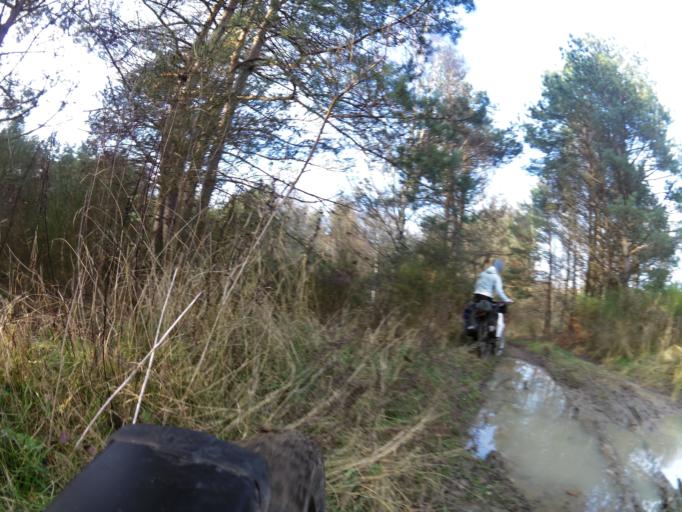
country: PL
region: West Pomeranian Voivodeship
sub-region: Powiat koszalinski
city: Polanow
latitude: 54.0792
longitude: 16.6606
